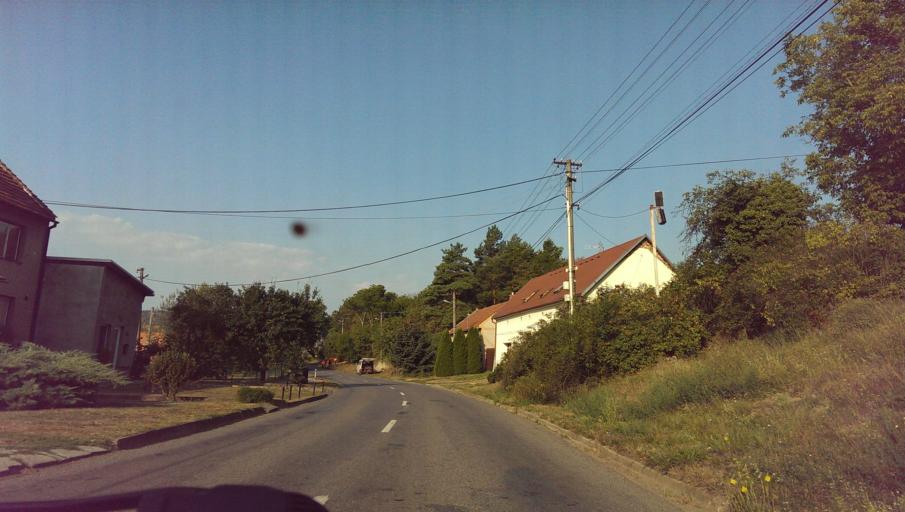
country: CZ
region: South Moravian
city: Nesovice
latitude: 49.1342
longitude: 17.1114
